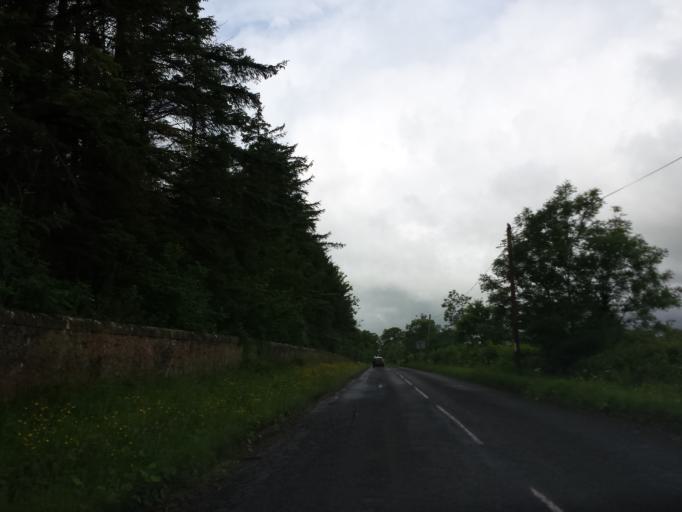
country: GB
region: Scotland
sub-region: Fife
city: Strathkinness
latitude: 56.3226
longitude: -2.8502
